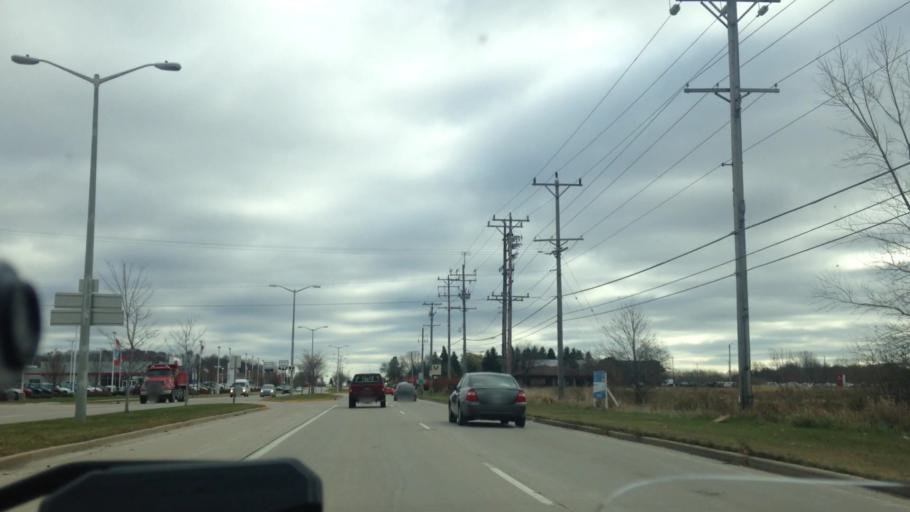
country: US
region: Wisconsin
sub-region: Washington County
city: West Bend
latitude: 43.4272
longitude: -88.2230
